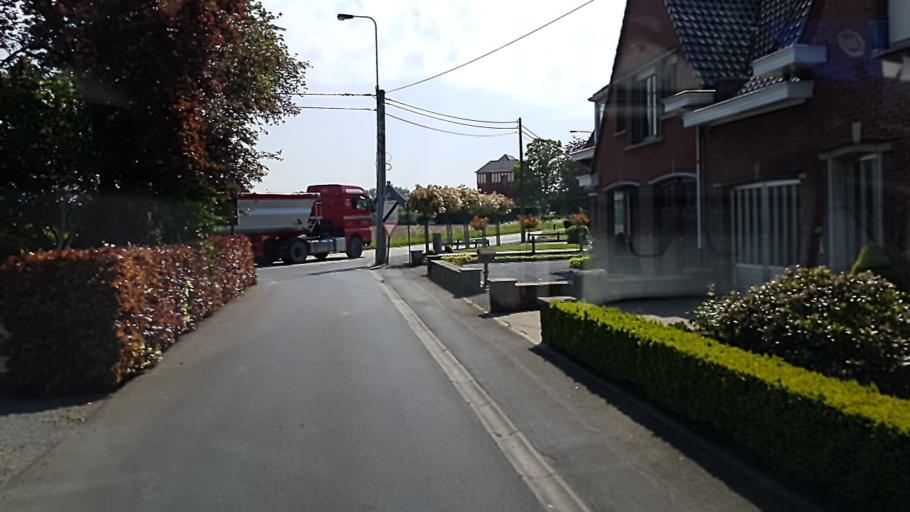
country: BE
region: Flanders
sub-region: Provincie West-Vlaanderen
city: Deerlijk
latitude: 50.8428
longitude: 3.4046
